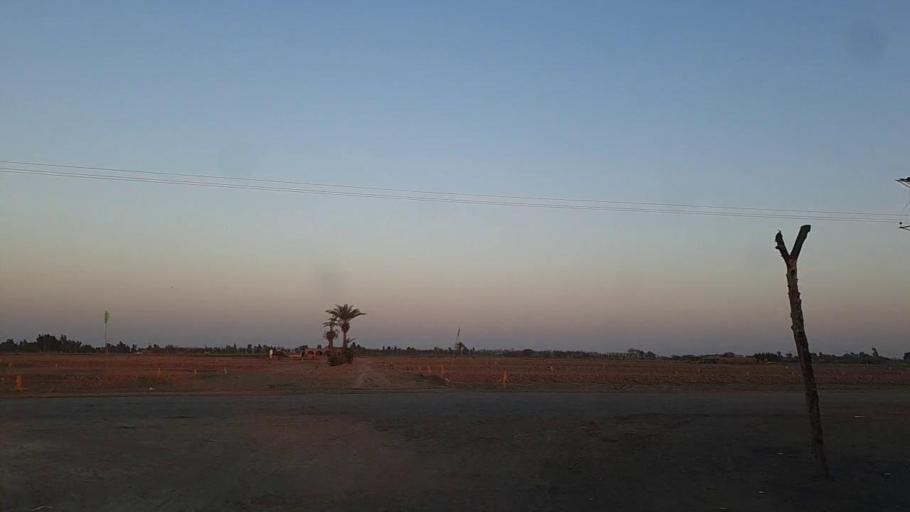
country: PK
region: Sindh
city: Samaro
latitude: 25.3092
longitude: 69.3898
